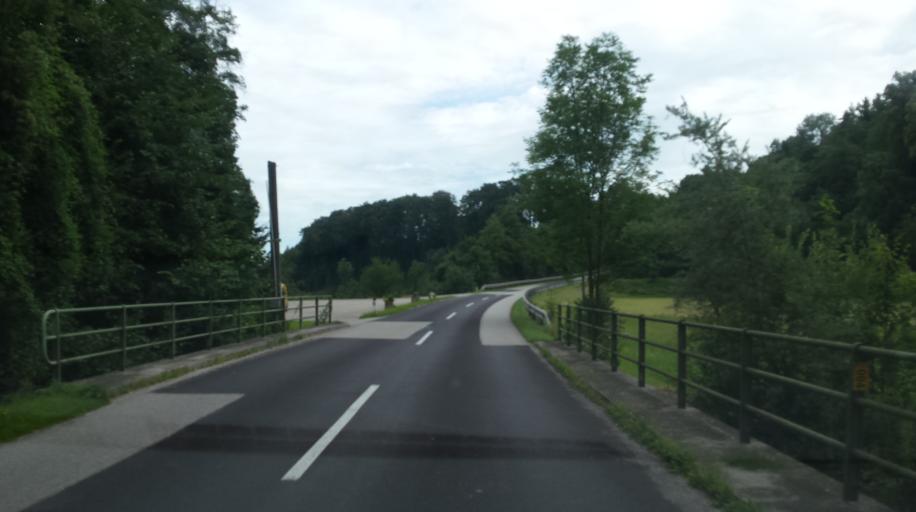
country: AT
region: Upper Austria
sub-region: Wels-Land
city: Bad Wimsbach-Neydharting
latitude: 48.0697
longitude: 13.9178
